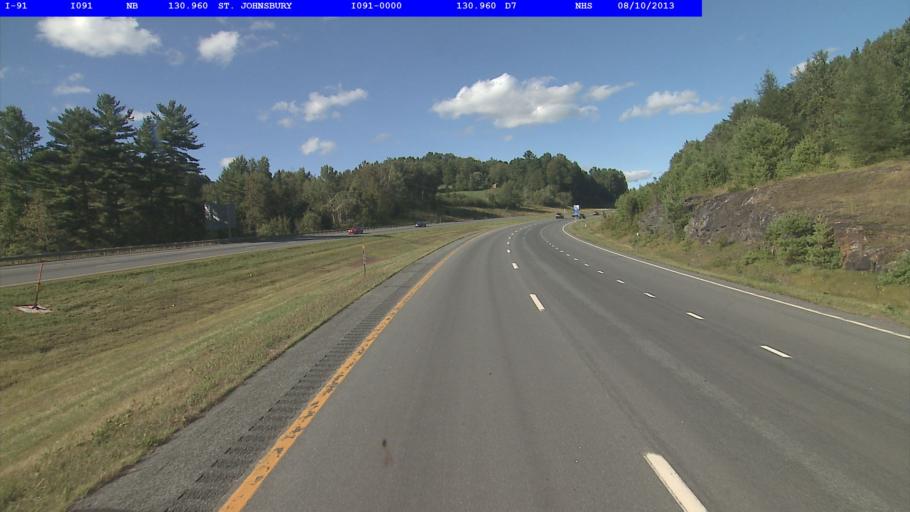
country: US
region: Vermont
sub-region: Caledonia County
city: St Johnsbury
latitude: 44.4330
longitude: -72.0338
